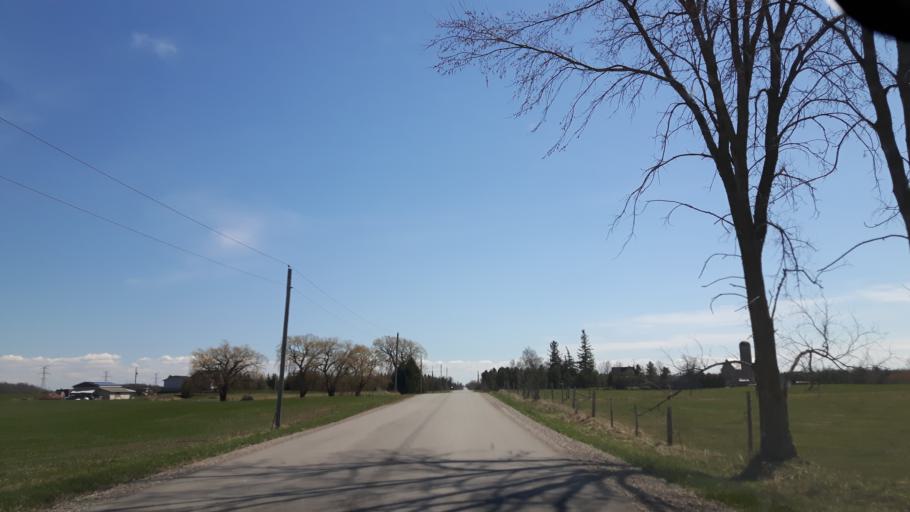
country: CA
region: Ontario
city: Goderich
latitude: 43.6165
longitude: -81.6439
